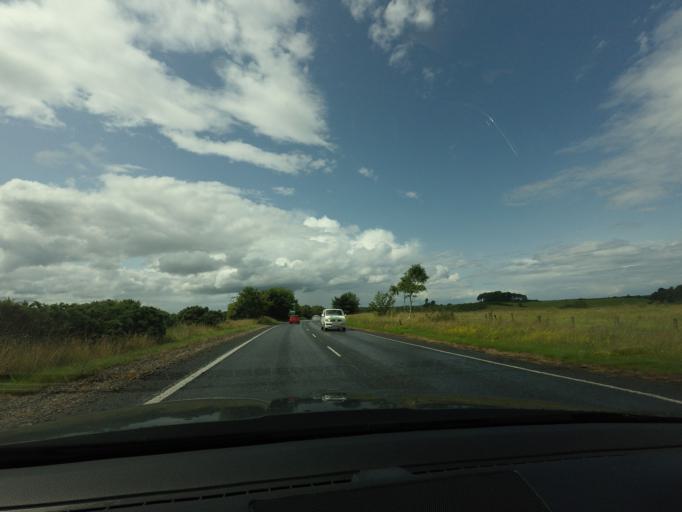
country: GB
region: Scotland
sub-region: Moray
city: Lhanbryd
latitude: 57.6343
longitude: -3.2293
